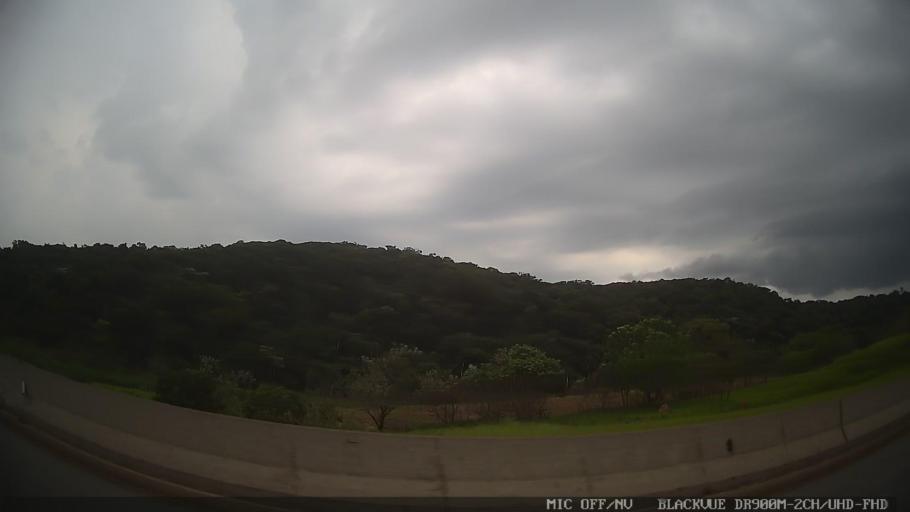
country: BR
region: Sao Paulo
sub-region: Jarinu
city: Jarinu
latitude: -23.0277
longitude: -46.7479
